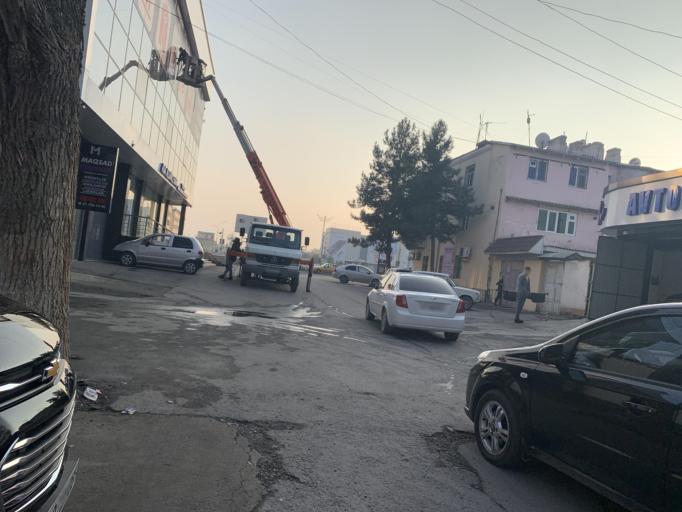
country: UZ
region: Fergana
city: Qo`qon
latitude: 40.5203
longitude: 70.9379
